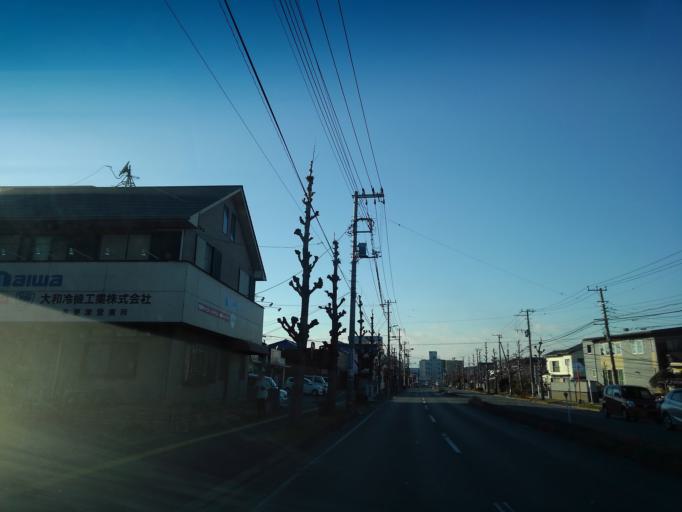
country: JP
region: Chiba
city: Kimitsu
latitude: 35.3327
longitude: 139.9018
